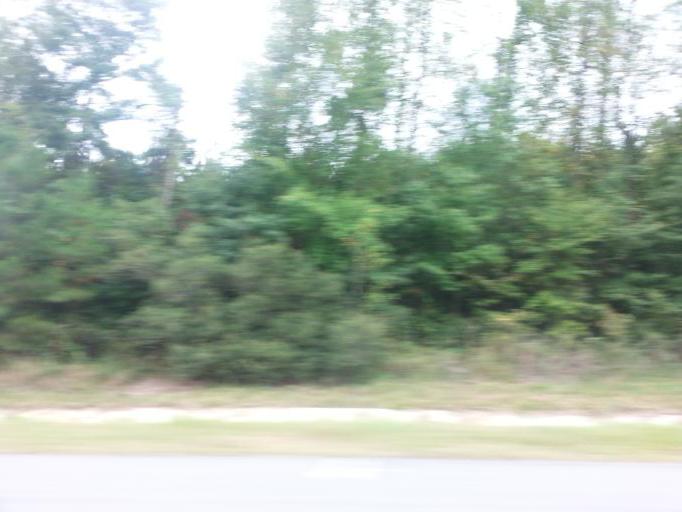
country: US
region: Alabama
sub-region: Conecuh County
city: Evergreen
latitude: 31.5347
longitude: -86.8940
